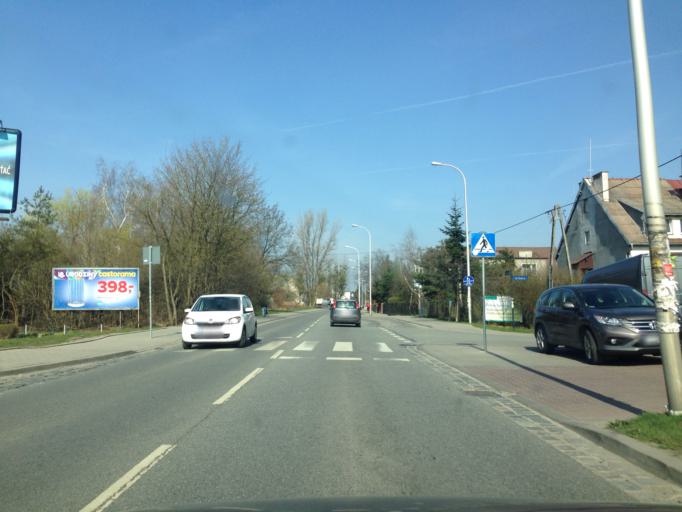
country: PL
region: Lower Silesian Voivodeship
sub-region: Powiat wroclawski
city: Wilczyce
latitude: 51.1049
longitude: 17.1464
